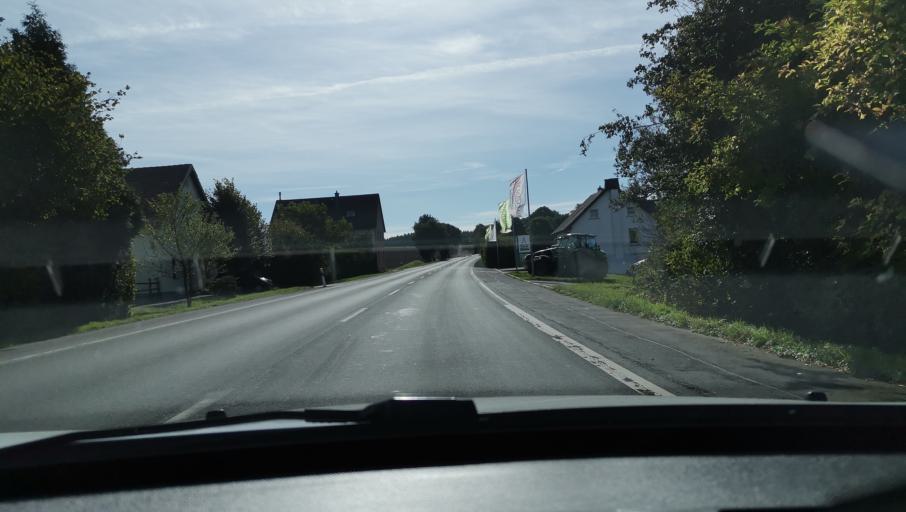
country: DE
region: North Rhine-Westphalia
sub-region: Regierungsbezirk Arnsberg
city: Breckerfeld
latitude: 51.2253
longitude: 7.4816
